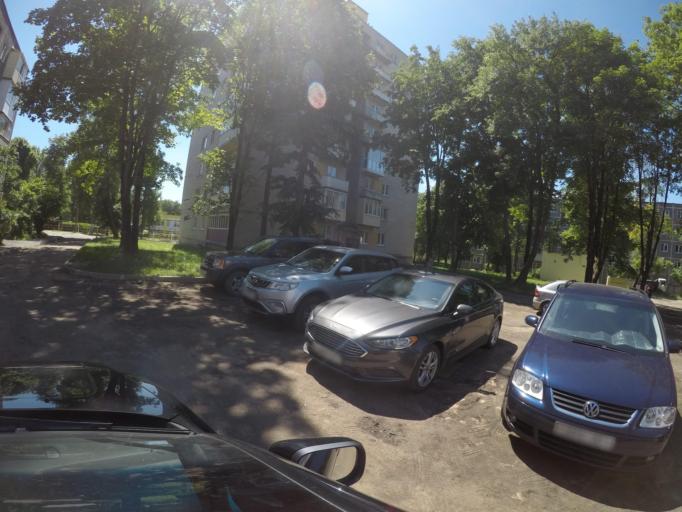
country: BY
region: Grodnenskaya
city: Hrodna
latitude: 53.6973
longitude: 23.8144
